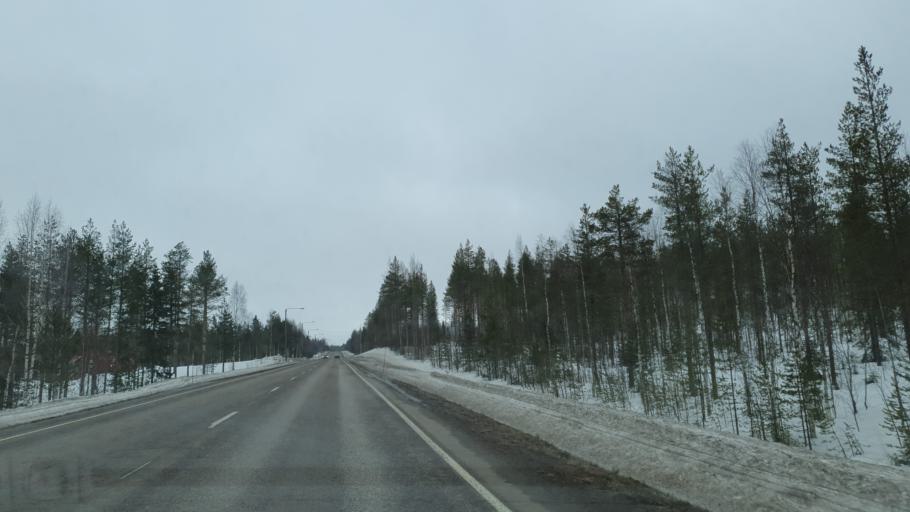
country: FI
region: Lapland
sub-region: Torniolaakso
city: Pello
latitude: 66.8796
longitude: 24.0673
